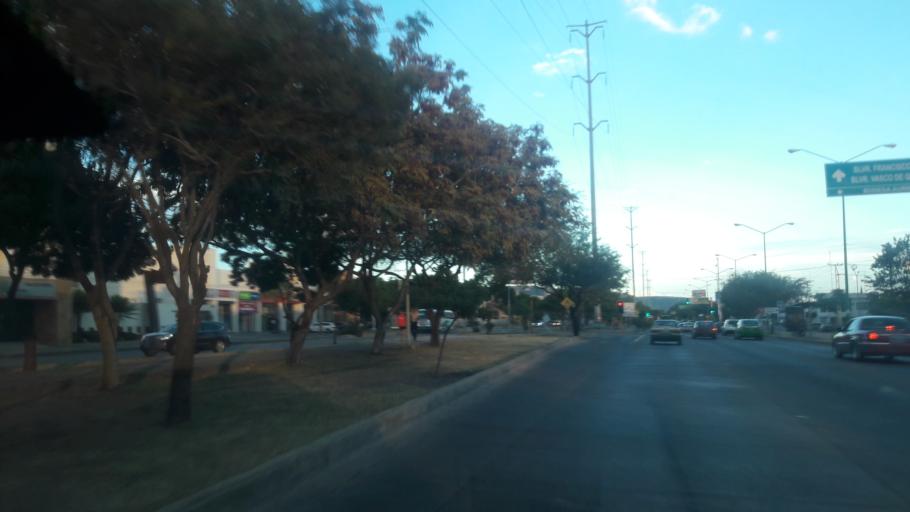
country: MX
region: Guanajuato
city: Leon
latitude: 21.1478
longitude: -101.6572
